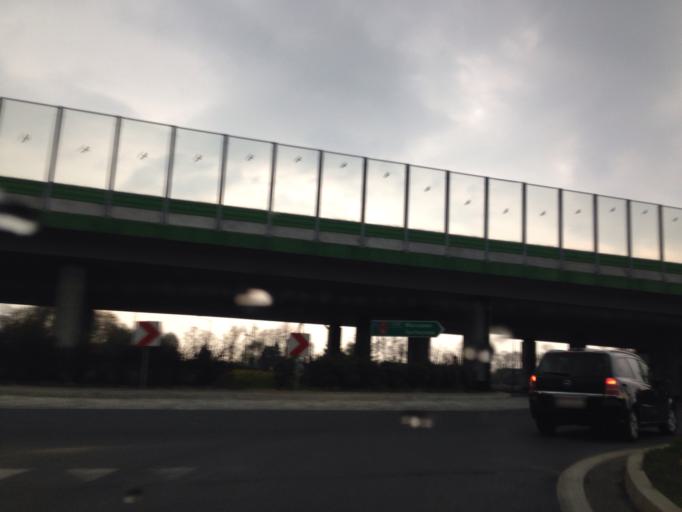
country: PL
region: Masovian Voivodeship
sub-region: Powiat plonski
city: Plonsk
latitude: 52.6313
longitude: 20.3825
